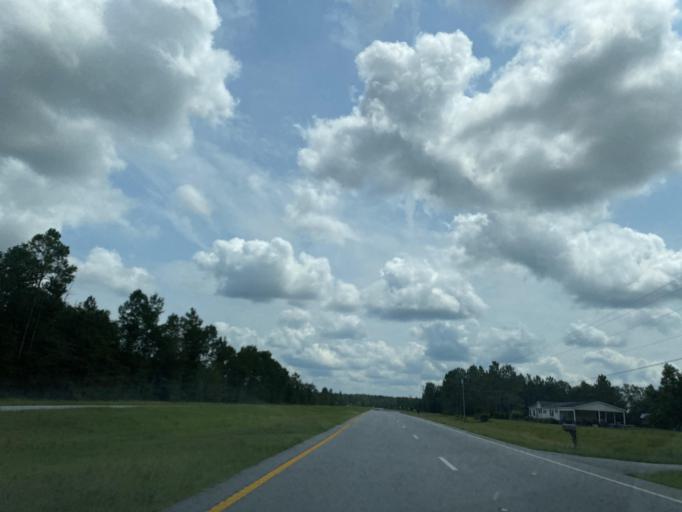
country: US
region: Georgia
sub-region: Ware County
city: Deenwood
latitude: 31.2856
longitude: -82.4514
